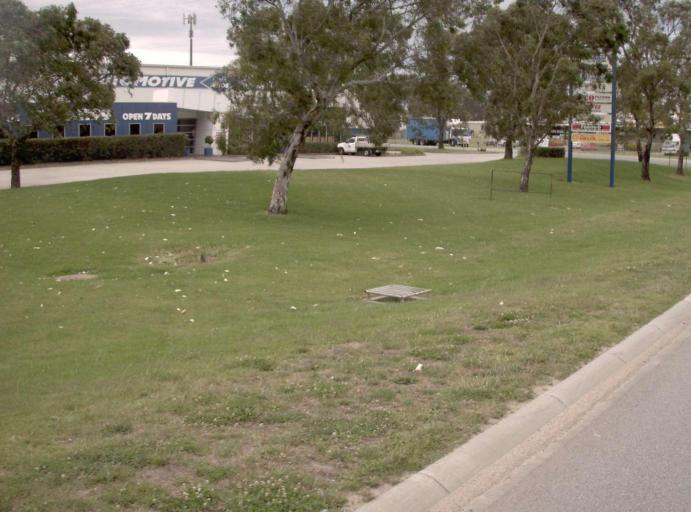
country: AU
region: Victoria
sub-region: Casey
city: Hampton Park
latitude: -38.0285
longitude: 145.2440
